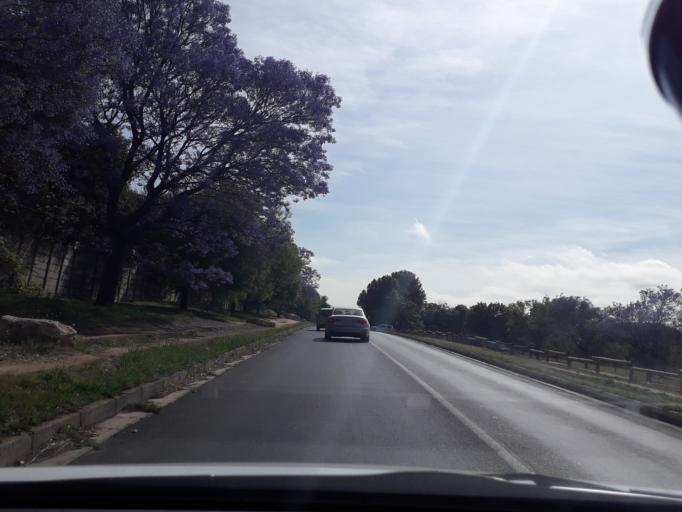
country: ZA
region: Gauteng
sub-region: City of Johannesburg Metropolitan Municipality
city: Roodepoort
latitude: -26.1124
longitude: 27.9483
